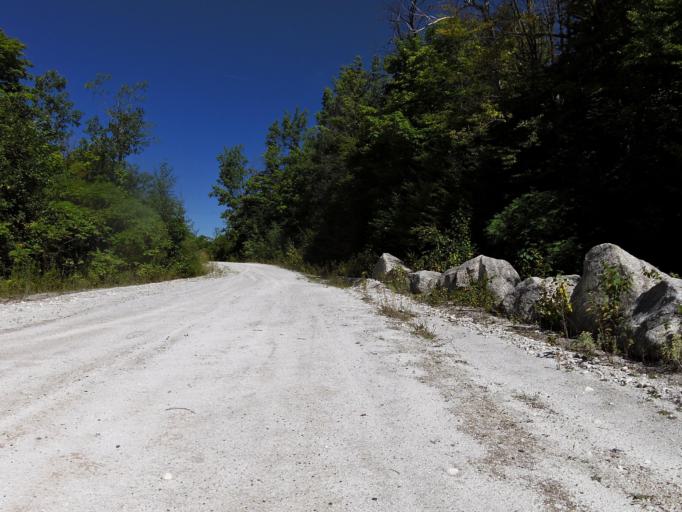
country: CA
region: Ontario
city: Arnprior
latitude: 45.1564
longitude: -76.4949
